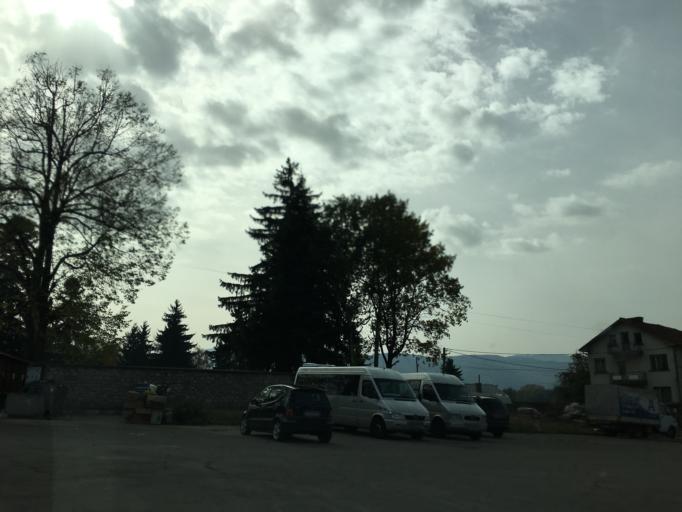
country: BG
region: Sofiya
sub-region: Obshtina Samokov
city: Samokov
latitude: 42.3252
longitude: 23.5594
